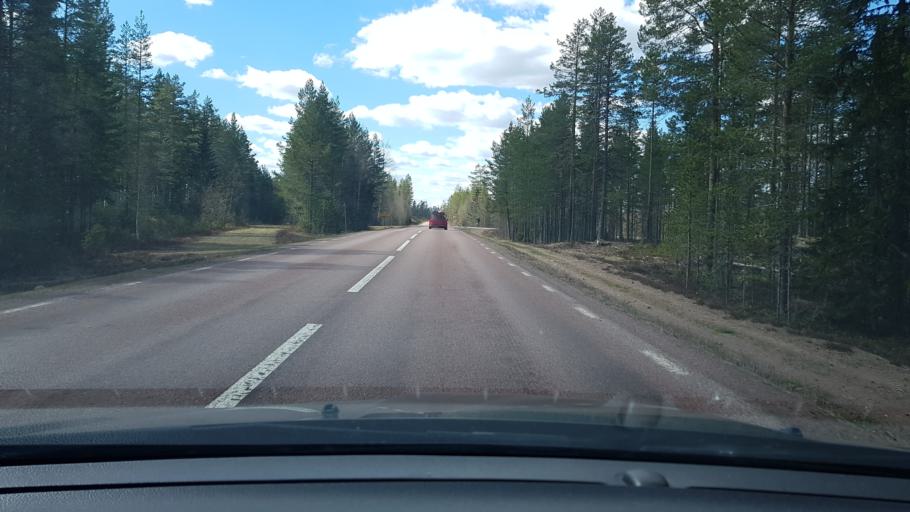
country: SE
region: Dalarna
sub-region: Alvdalens Kommun
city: AElvdalen
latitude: 61.1112
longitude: 13.8518
